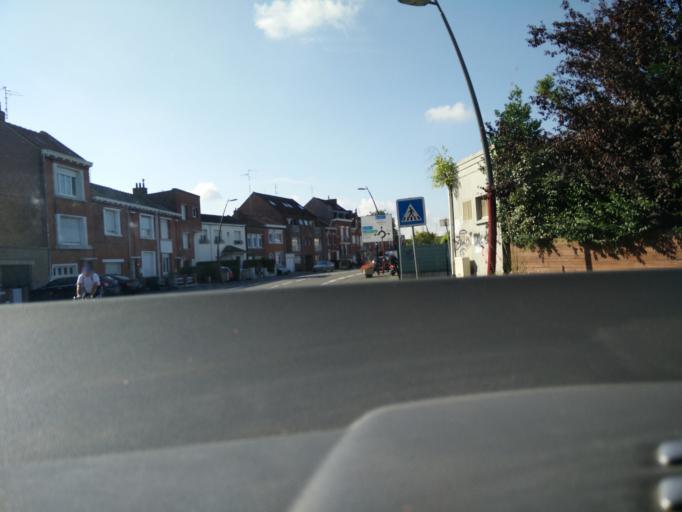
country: FR
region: Nord-Pas-de-Calais
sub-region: Departement du Nord
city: Wambrechies
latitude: 50.6807
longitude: 3.0476
